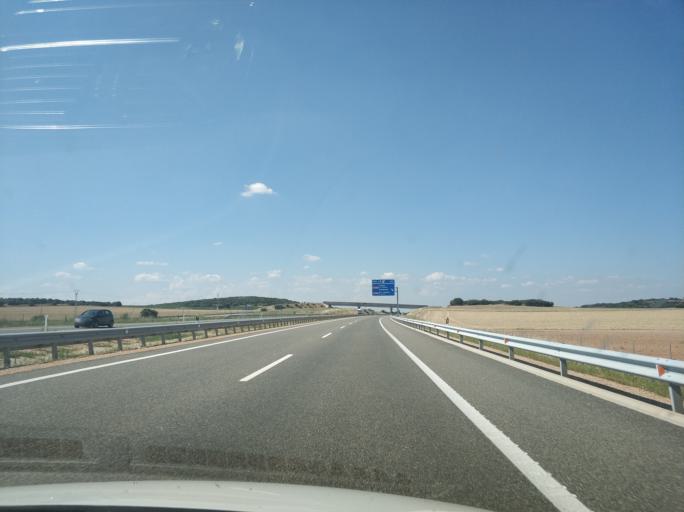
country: ES
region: Castille and Leon
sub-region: Provincia de Zamora
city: Montamarta
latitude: 41.6776
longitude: -5.8047
